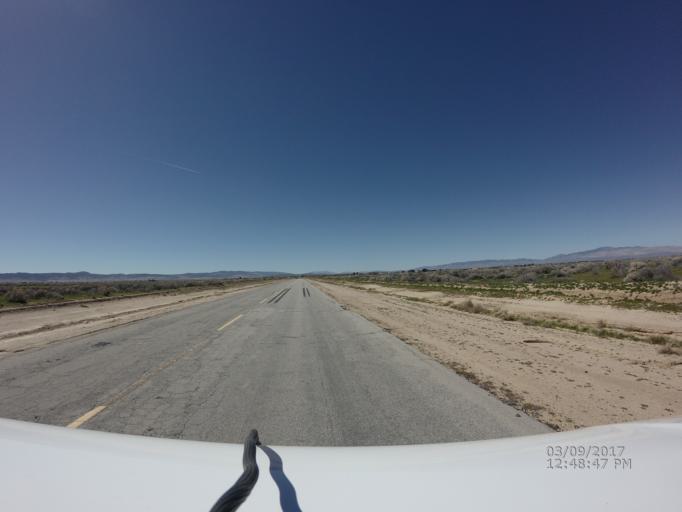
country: US
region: California
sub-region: Los Angeles County
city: Quartz Hill
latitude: 34.7475
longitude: -118.2596
